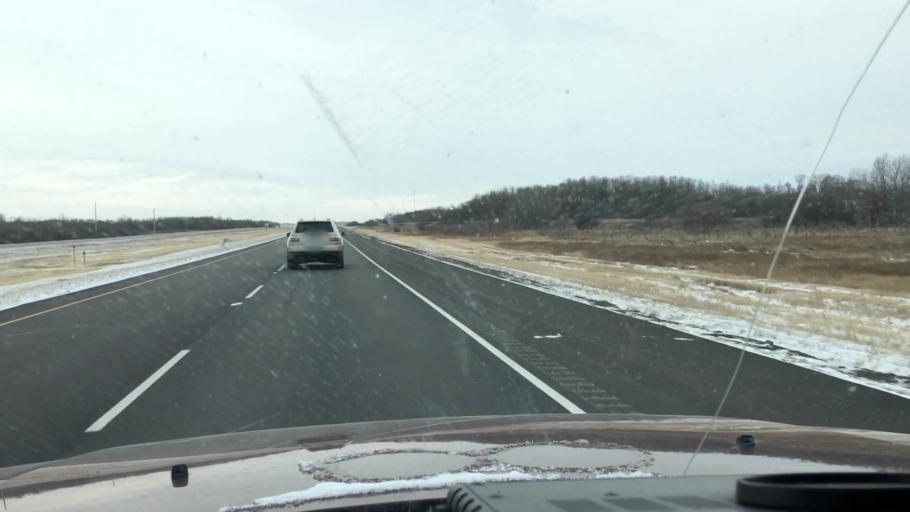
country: CA
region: Saskatchewan
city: Saskatoon
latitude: 51.8805
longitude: -106.5123
